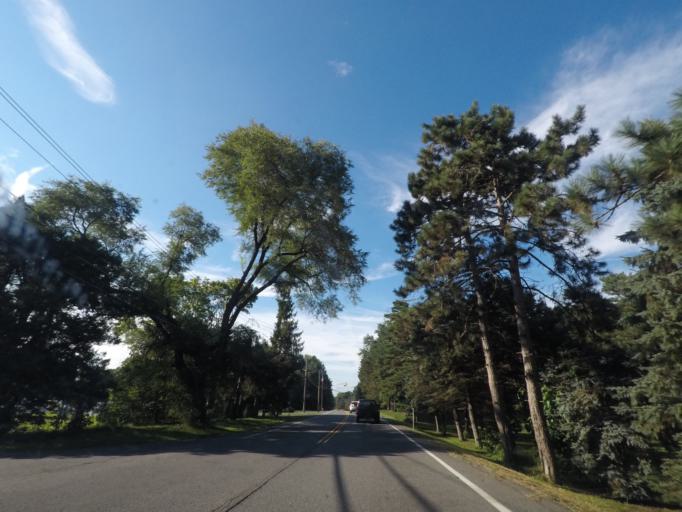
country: US
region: New York
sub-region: Albany County
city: West Albany
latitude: 42.7237
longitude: -73.7720
